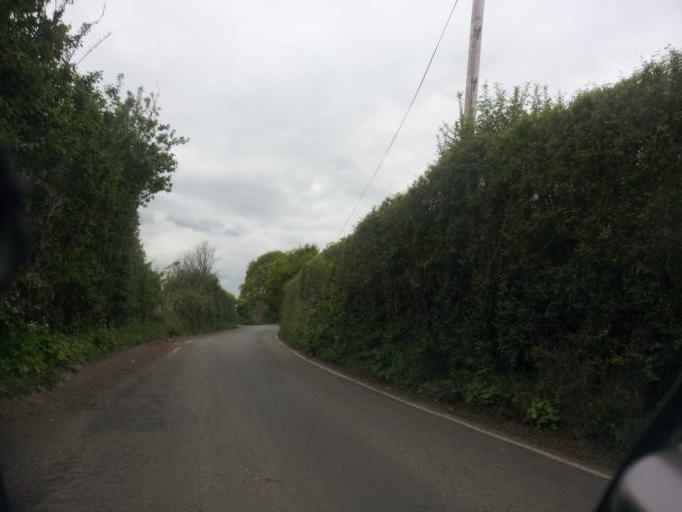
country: GB
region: England
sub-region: Kent
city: Newington
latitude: 51.3780
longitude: 0.6906
